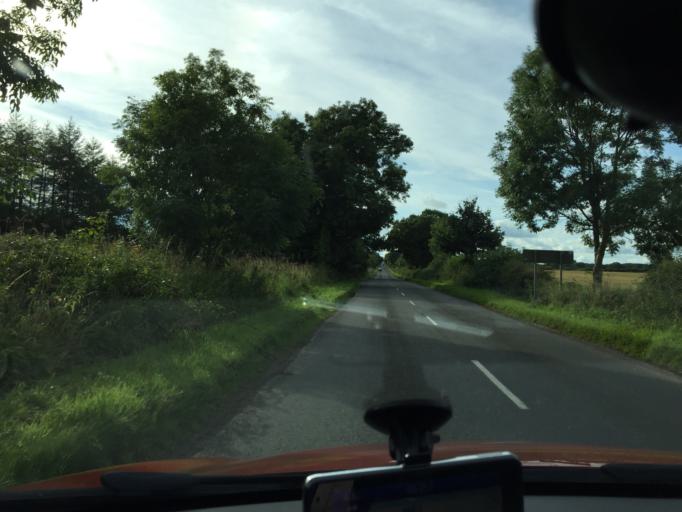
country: GB
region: Scotland
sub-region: Dumfries and Galloway
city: Gretna
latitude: 55.0060
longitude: -3.0663
